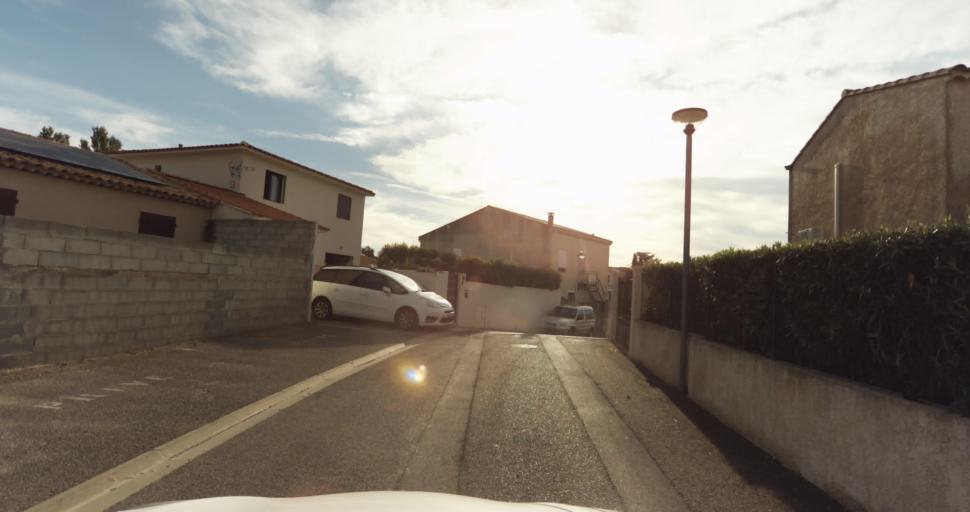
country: FR
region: Provence-Alpes-Cote d'Azur
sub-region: Departement des Bouches-du-Rhone
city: Miramas
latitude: 43.5819
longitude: 5.0122
